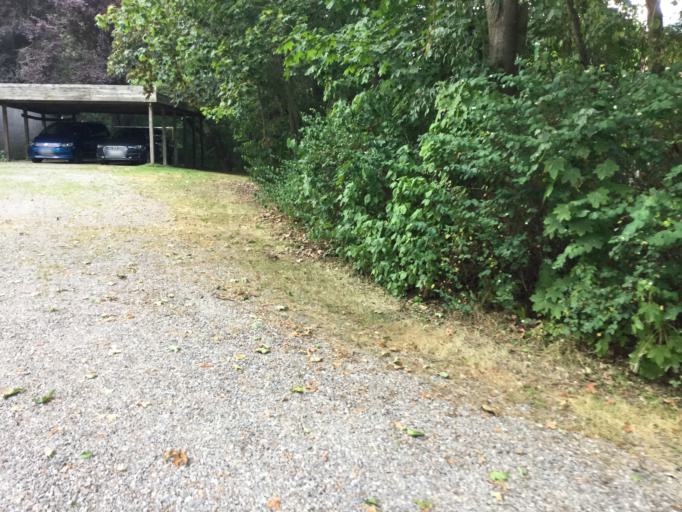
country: DE
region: Mecklenburg-Vorpommern
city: Jordenstorf
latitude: 53.8261
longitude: 12.6943
